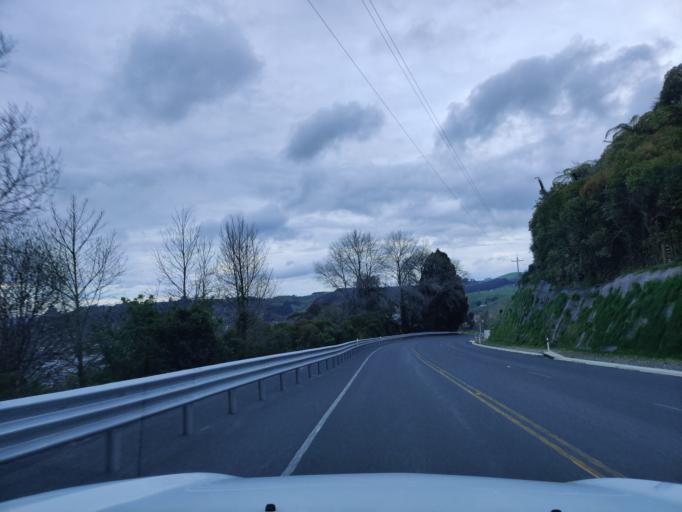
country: NZ
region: Waikato
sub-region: Otorohanga District
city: Otorohanga
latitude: -38.3505
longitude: 175.1619
